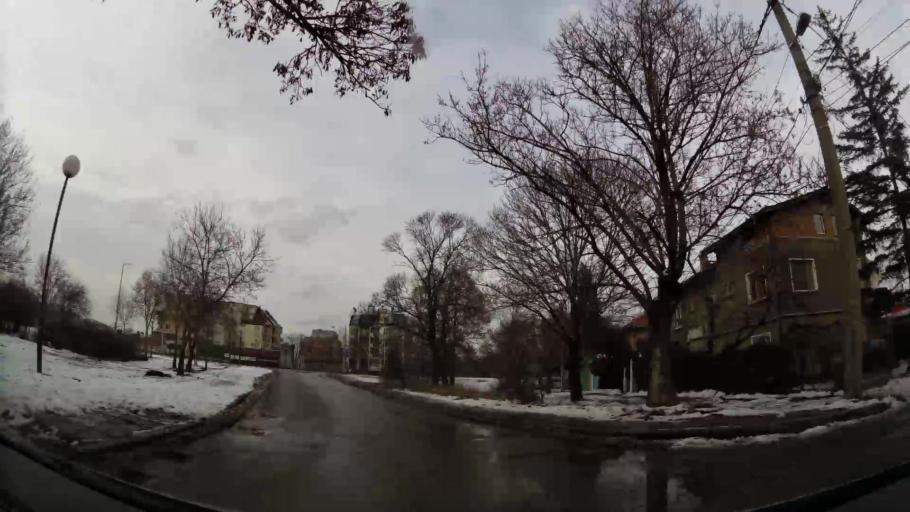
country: BG
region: Sofia-Capital
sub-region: Stolichna Obshtina
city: Sofia
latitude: 42.7003
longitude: 23.3755
